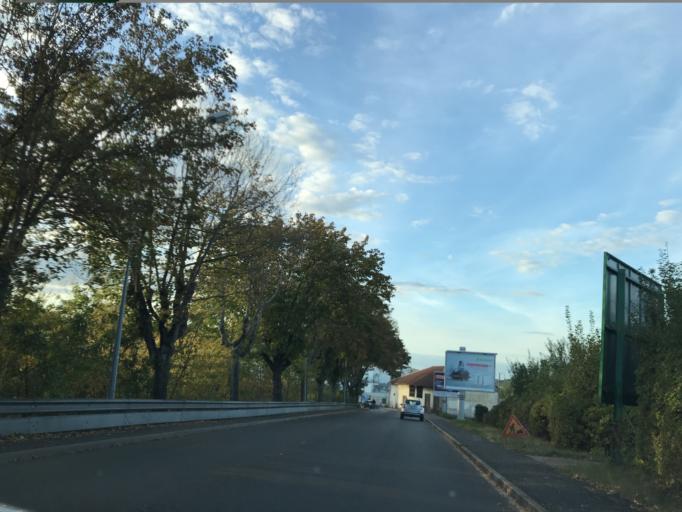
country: FR
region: Auvergne
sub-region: Departement de l'Allier
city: Vichy
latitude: 46.1186
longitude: 3.4347
